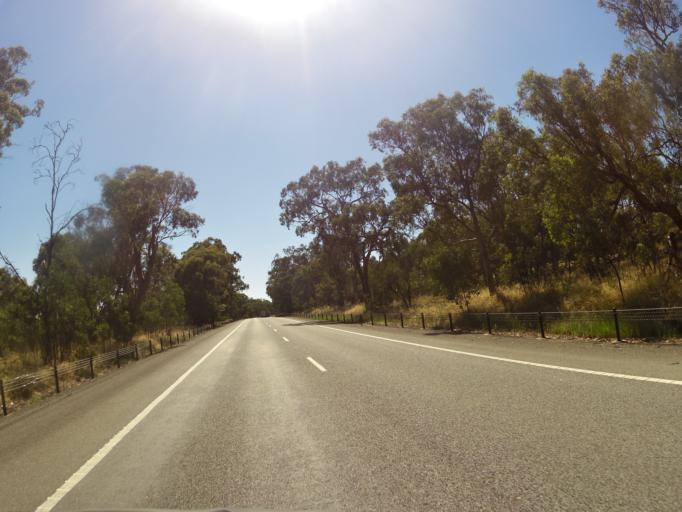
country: AU
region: Victoria
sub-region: Greater Shepparton
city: Shepparton
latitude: -36.7723
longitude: 145.5187
